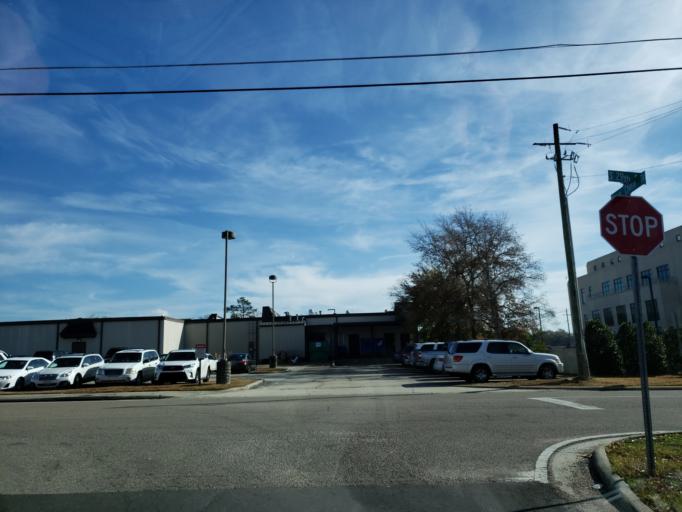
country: US
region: Mississippi
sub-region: Lamar County
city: Arnold Line
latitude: 31.3235
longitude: -89.3327
